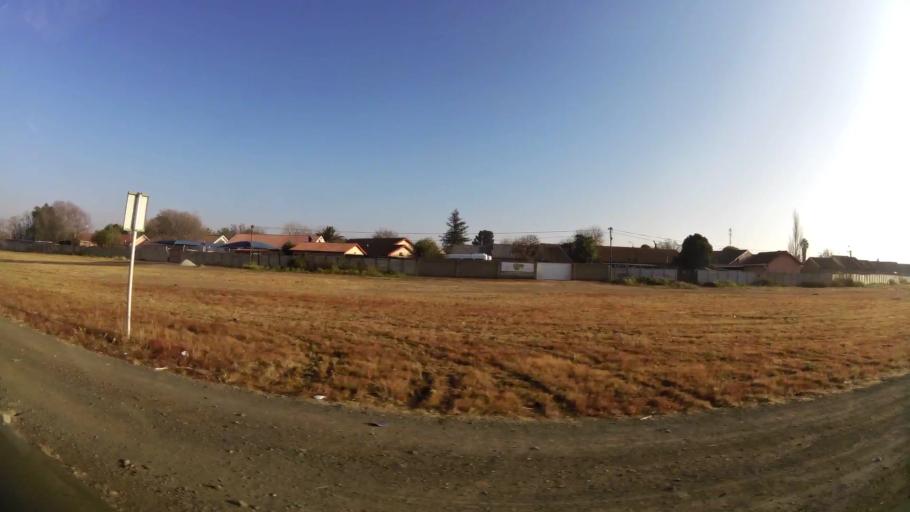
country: ZA
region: Orange Free State
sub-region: Mangaung Metropolitan Municipality
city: Bloemfontein
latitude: -29.1684
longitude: 26.1975
